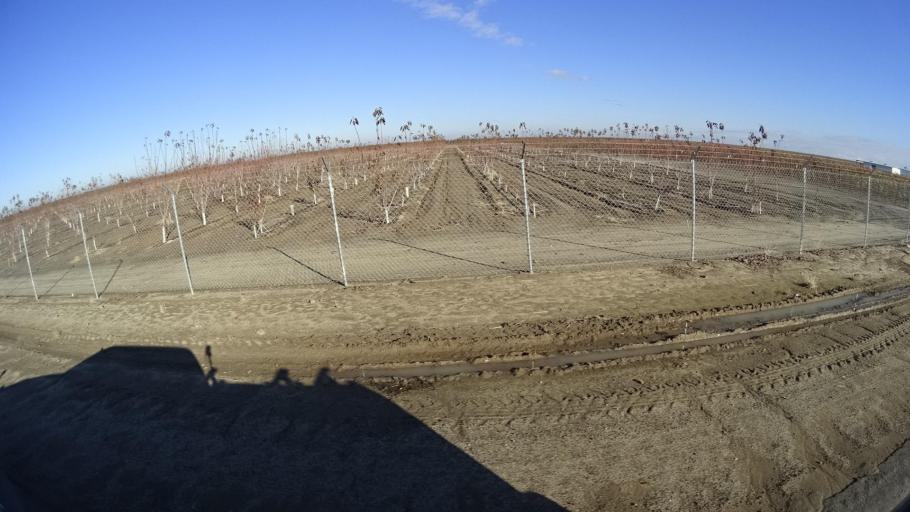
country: US
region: California
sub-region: Kern County
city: McFarland
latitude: 35.6889
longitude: -119.3076
